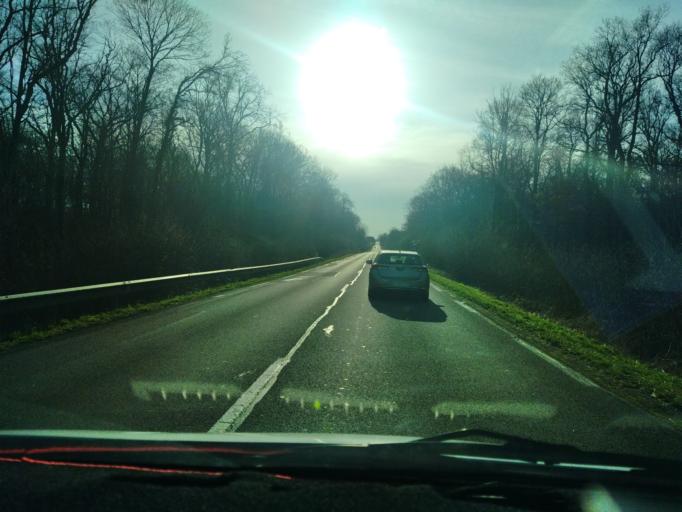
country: FR
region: Franche-Comte
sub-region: Departement de la Haute-Saone
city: Gray
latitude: 47.3824
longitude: 5.6592
